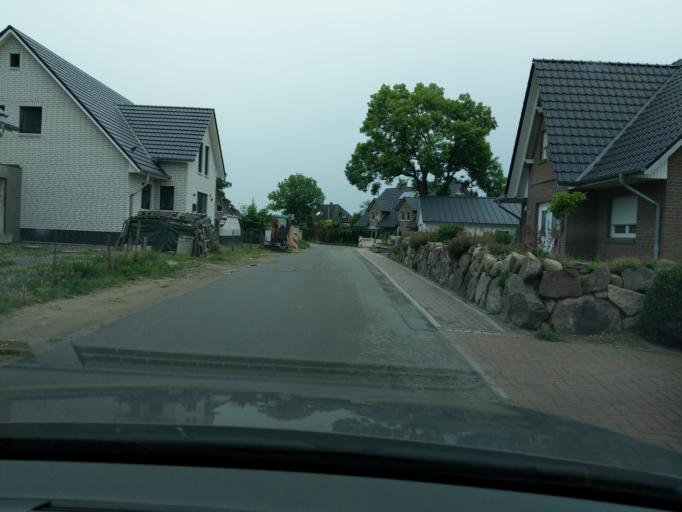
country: DE
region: Schleswig-Holstein
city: Schnakenbek
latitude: 53.3849
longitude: 10.5009
